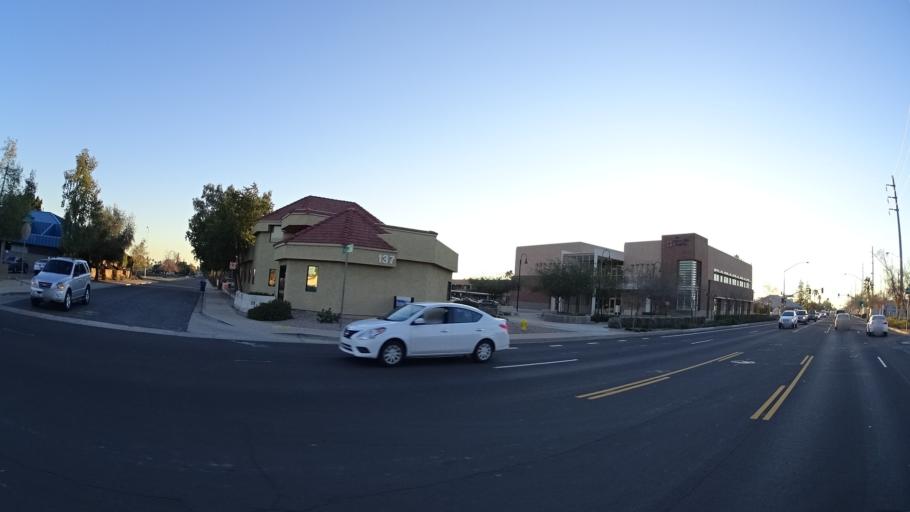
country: US
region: Arizona
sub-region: Maricopa County
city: Mesa
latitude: 33.4223
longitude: -111.8272
